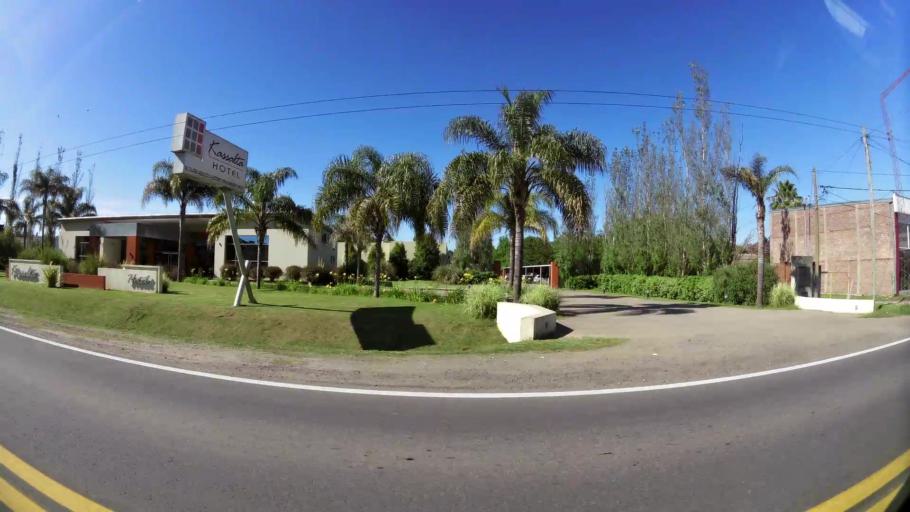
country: AR
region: Santa Fe
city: Esperanza
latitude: -31.4489
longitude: -60.9038
